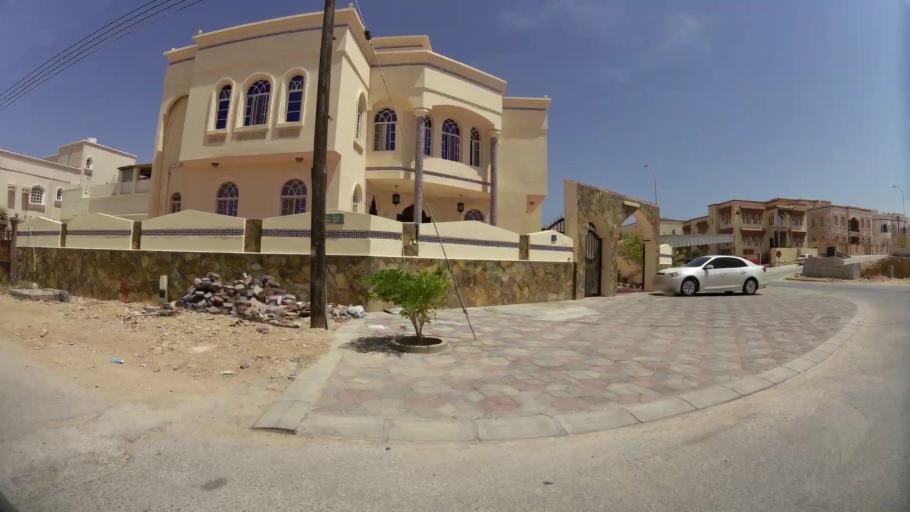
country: OM
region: Zufar
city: Salalah
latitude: 17.0569
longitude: 54.1619
